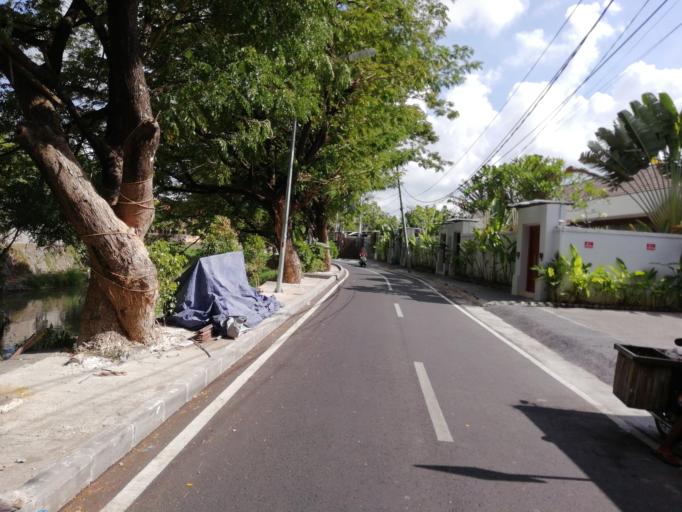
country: ID
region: Bali
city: Kuta
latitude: -8.7072
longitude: 115.1763
